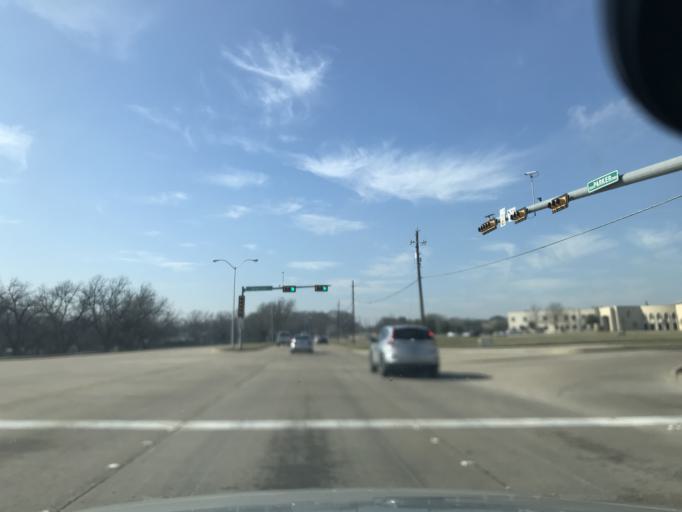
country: US
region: Texas
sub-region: Collin County
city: Plano
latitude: 33.0435
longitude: -96.6671
